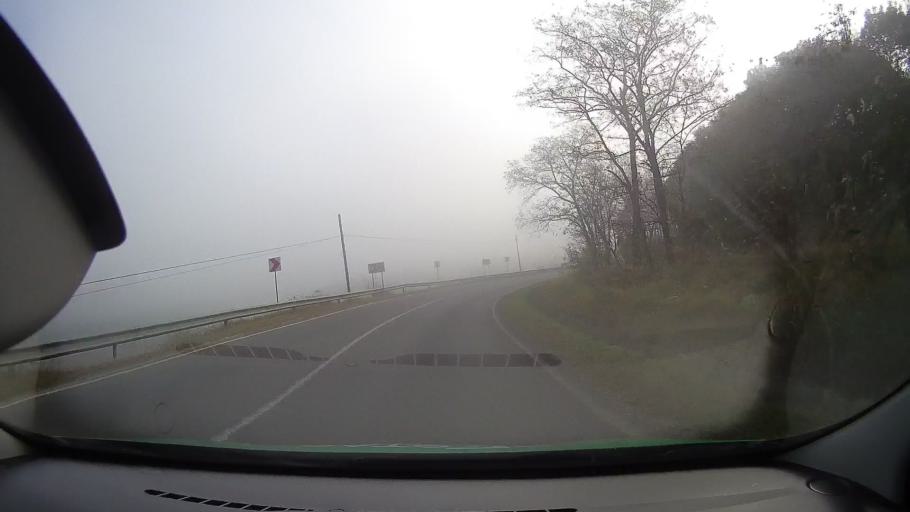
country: RO
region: Tulcea
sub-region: Municipiul Tulcea
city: Tulcea
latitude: 45.1668
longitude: 28.8397
